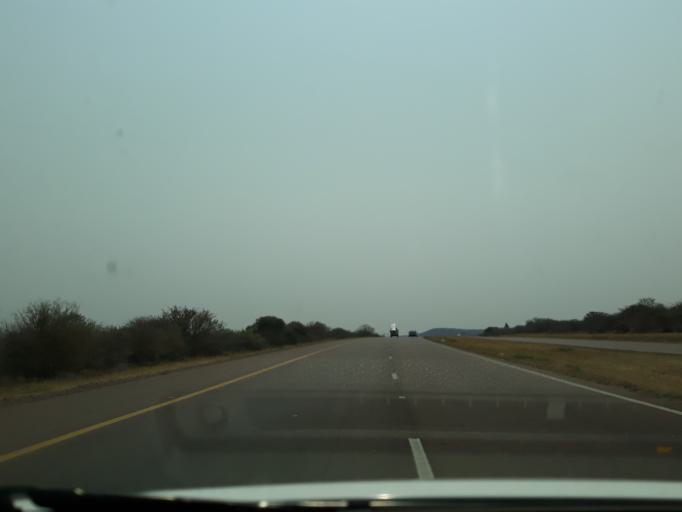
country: BW
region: Kgatleng
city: Bokaa
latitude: -24.4156
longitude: 26.0491
